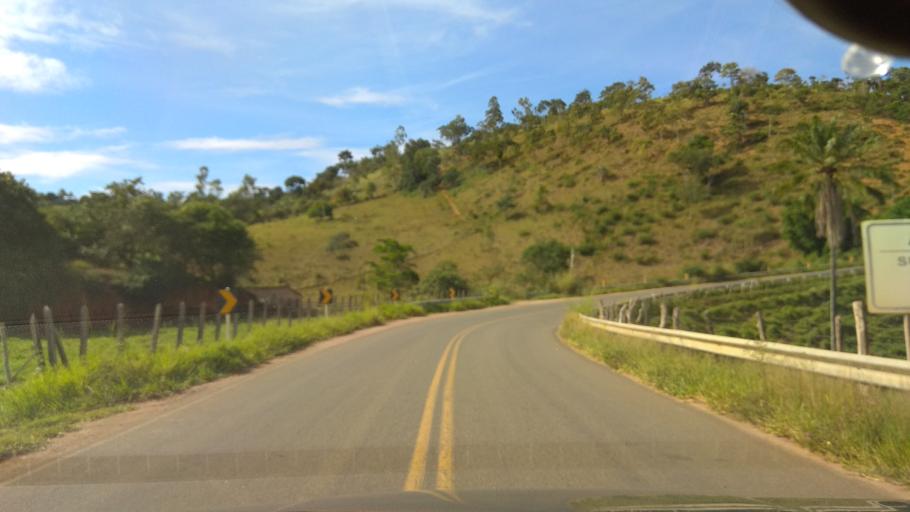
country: BR
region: Bahia
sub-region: Ubaira
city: Ubaira
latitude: -13.2531
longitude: -39.6643
